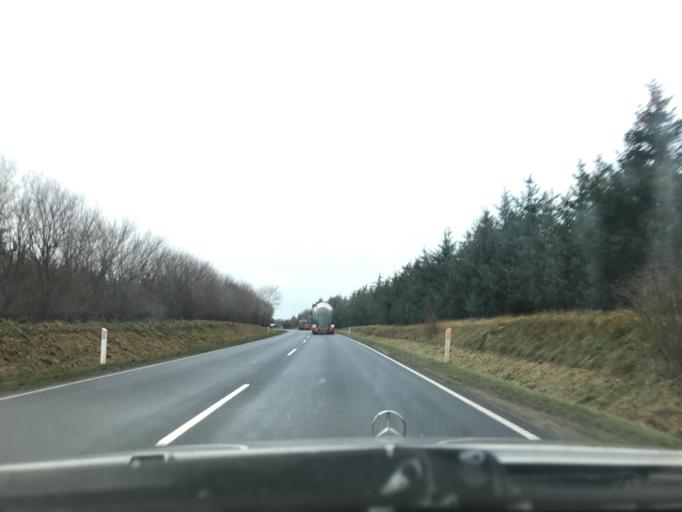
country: DK
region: South Denmark
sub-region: Esbjerg Kommune
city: Ribe
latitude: 55.2785
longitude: 8.8587
